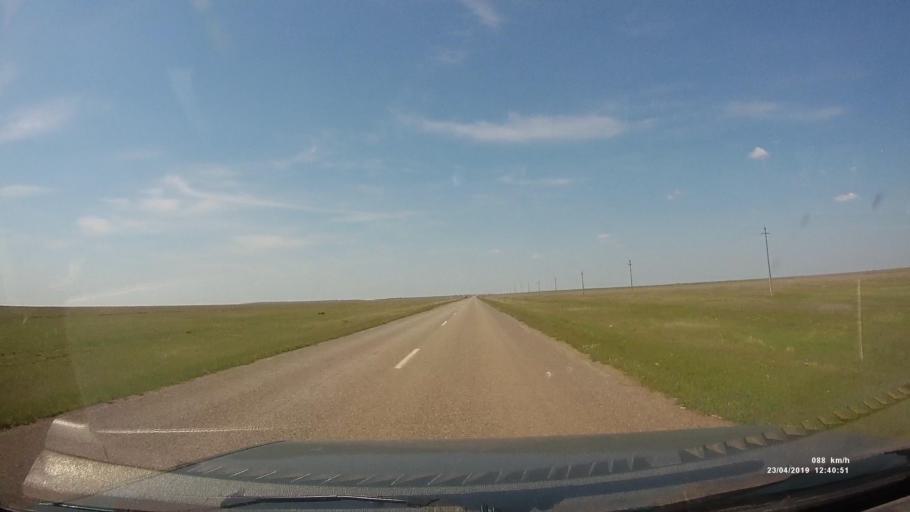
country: RU
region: Kalmykiya
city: Yashalta
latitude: 46.4437
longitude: 42.6898
